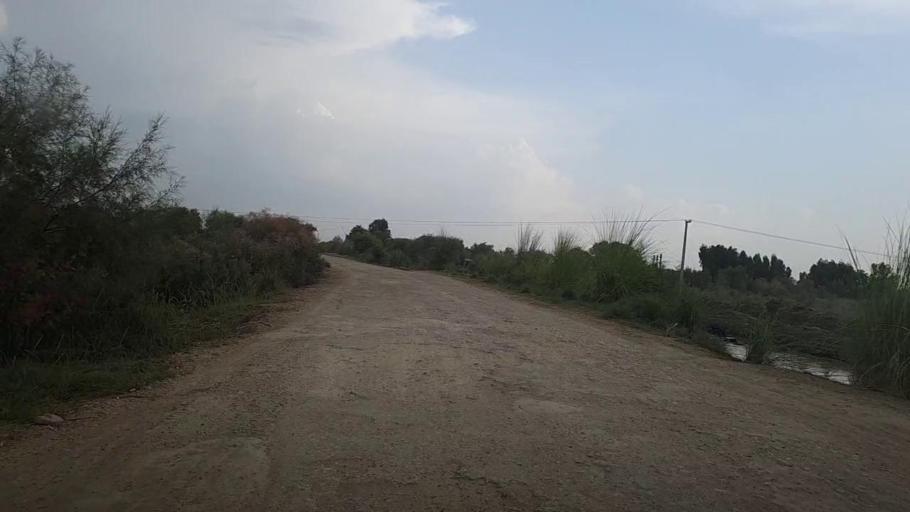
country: PK
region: Sindh
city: Khanpur
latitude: 27.8407
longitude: 69.4846
